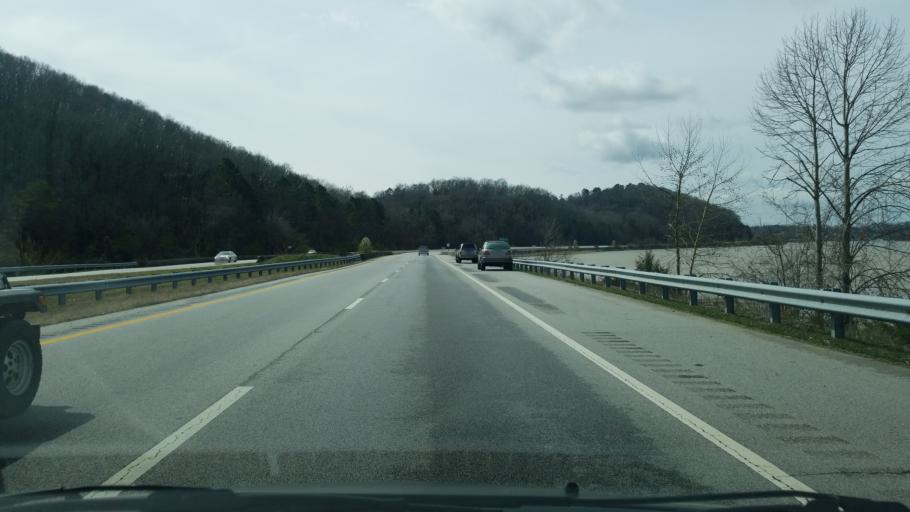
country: US
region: Tennessee
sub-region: Hamilton County
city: Harrison
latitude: 35.1497
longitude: -85.1091
